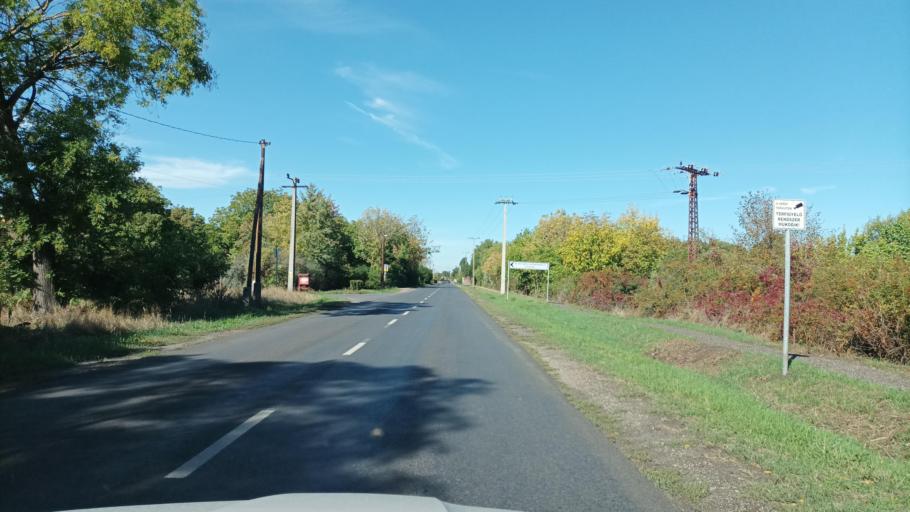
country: HU
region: Pest
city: Cegled
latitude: 47.1658
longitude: 19.8356
